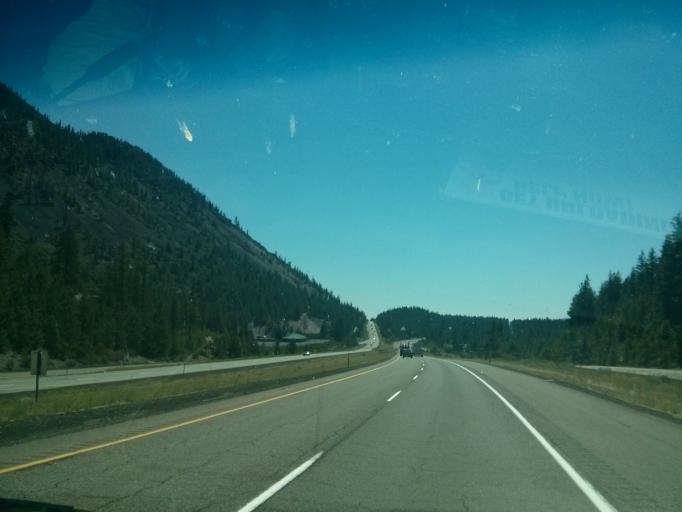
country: US
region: California
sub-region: Siskiyou County
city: Weed
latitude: 41.3718
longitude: -122.3738
